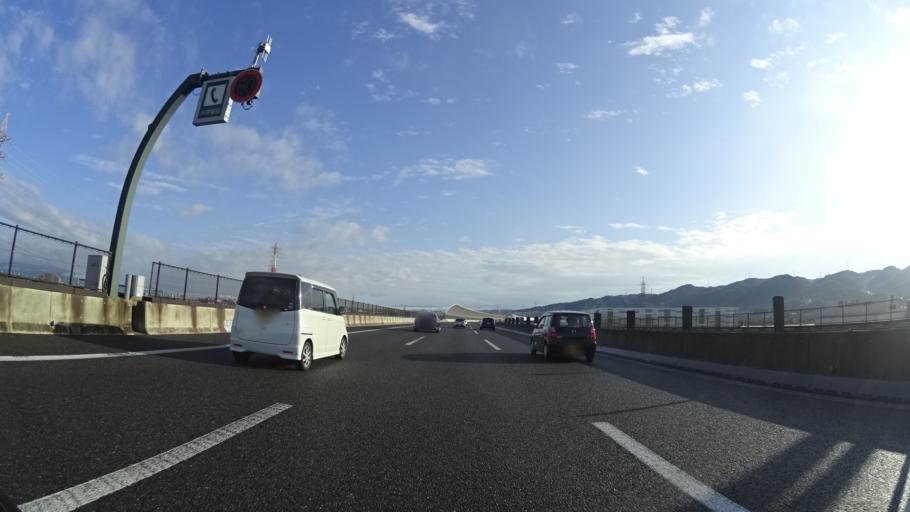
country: JP
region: Osaka
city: Hirakata
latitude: 34.7772
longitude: 135.6666
